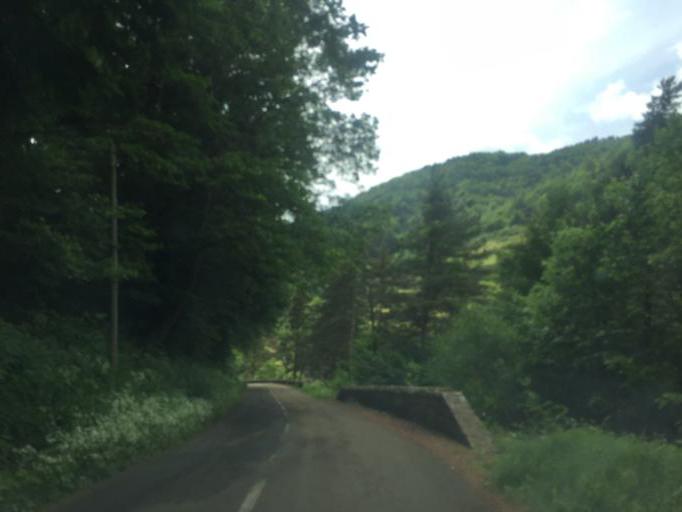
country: FR
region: Rhone-Alpes
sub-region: Departement de l'Ardeche
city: Saint-Priest
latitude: 44.6963
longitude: 4.5408
